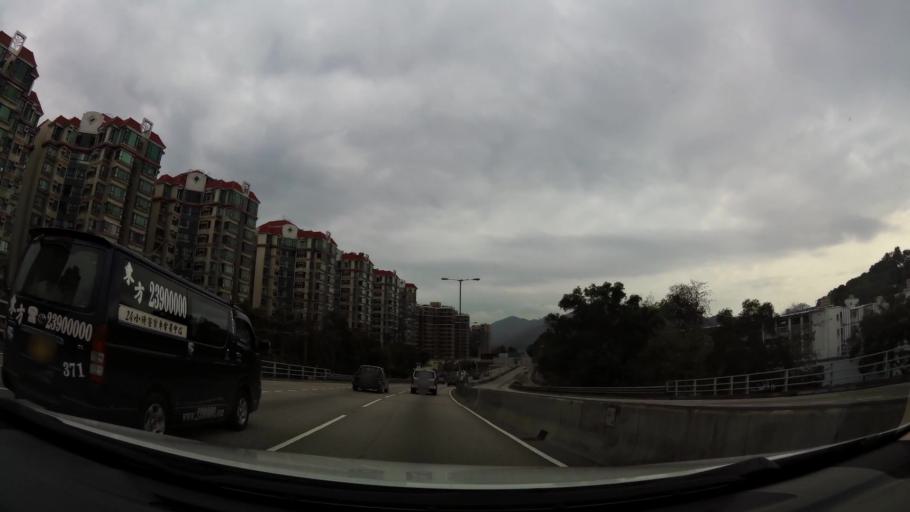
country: HK
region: Yuen Long
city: Yuen Long Kau Hui
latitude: 22.4435
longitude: 114.0168
